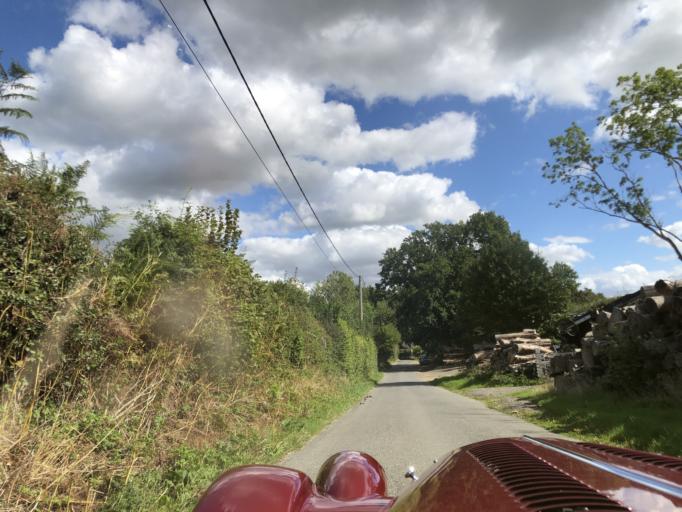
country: GB
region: England
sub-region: East Sussex
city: Northiam
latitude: 50.9951
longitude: 0.5673
